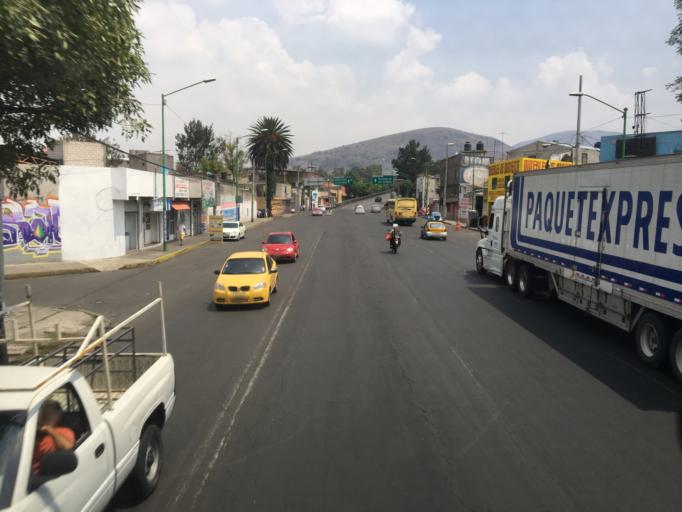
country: MX
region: Mexico
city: Tlalnepantla
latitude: 19.5231
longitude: -99.1581
